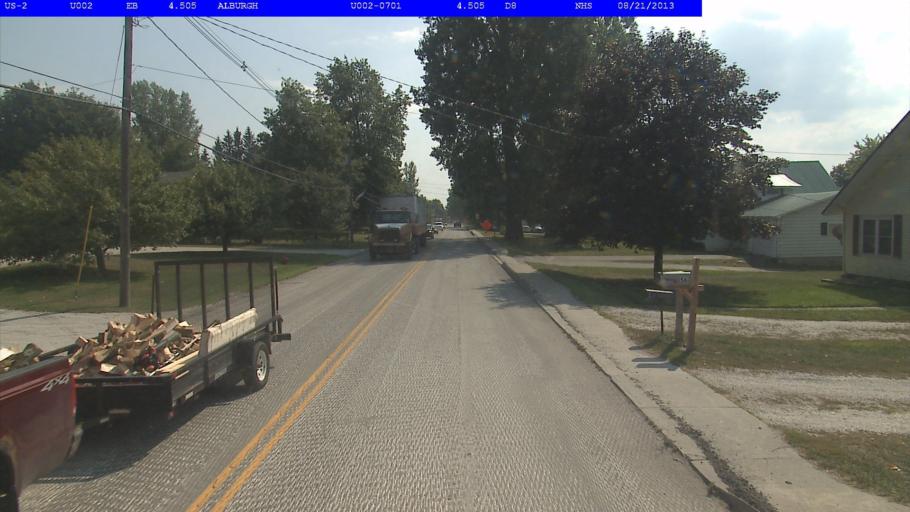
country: US
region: New York
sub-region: Clinton County
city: Rouses Point
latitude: 44.9694
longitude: -73.3026
